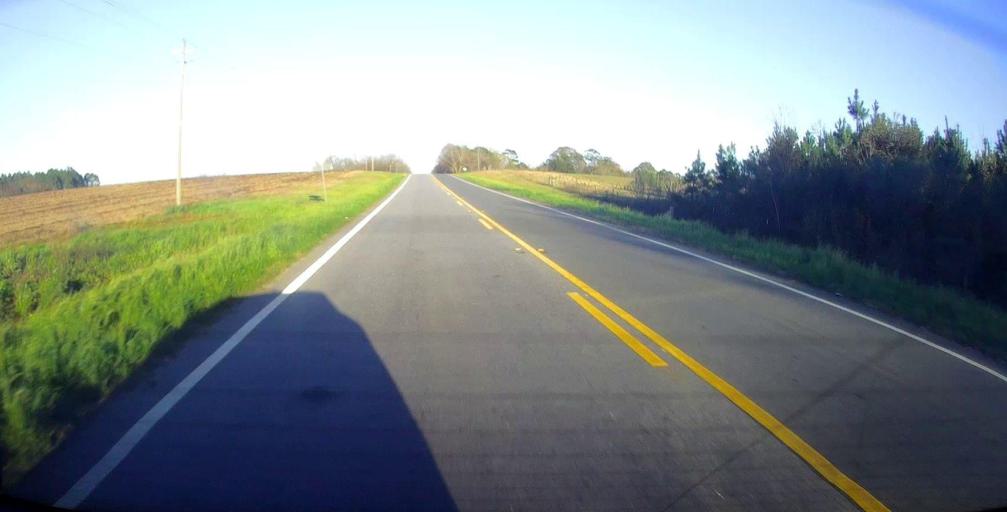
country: US
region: Georgia
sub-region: Wilcox County
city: Rochelle
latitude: 31.9608
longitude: -83.4177
